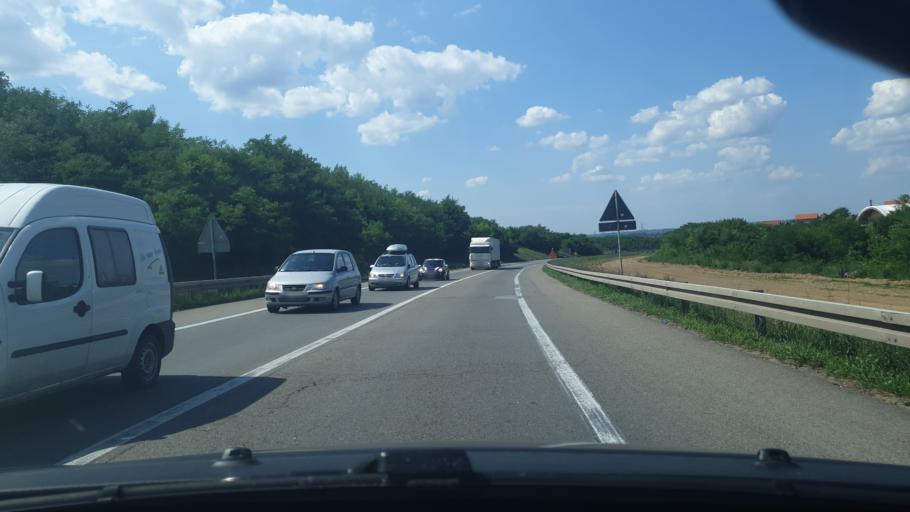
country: RS
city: Ostruznica
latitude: 44.7136
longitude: 20.3633
